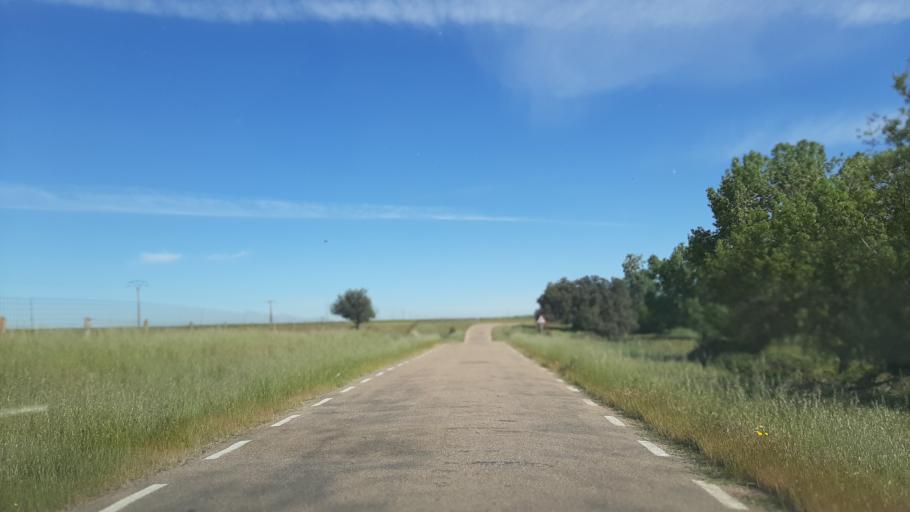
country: ES
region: Castille and Leon
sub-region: Provincia de Salamanca
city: Gajates
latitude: 40.7921
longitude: -5.3722
